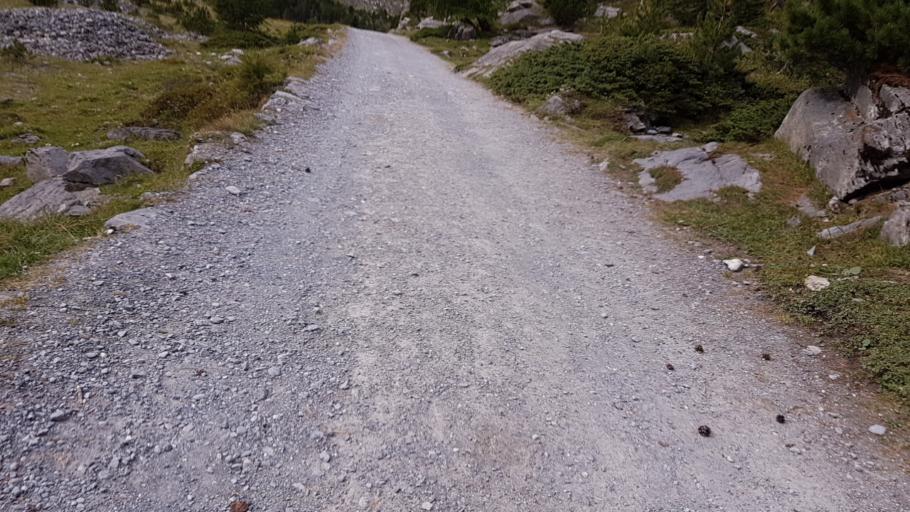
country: CH
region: Bern
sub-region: Frutigen-Niedersimmental District
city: Kandersteg
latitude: 46.4419
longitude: 7.6385
